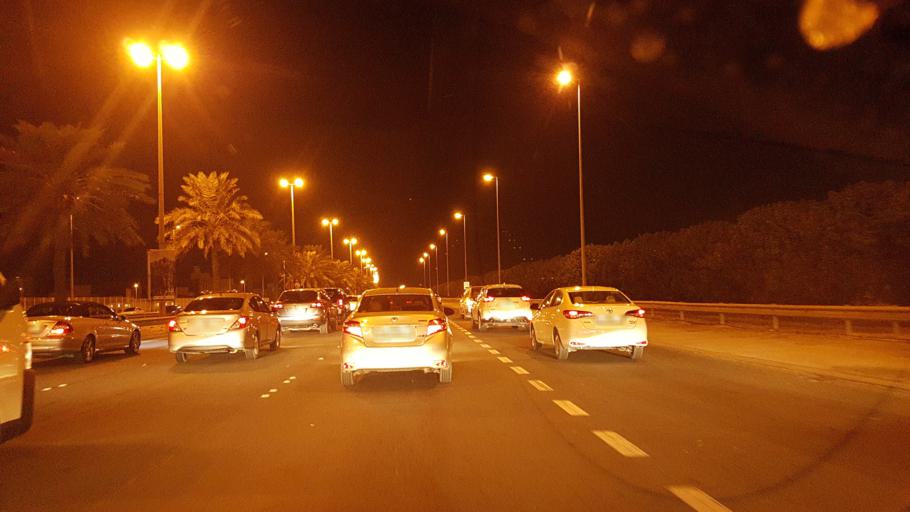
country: BH
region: Central Governorate
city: Madinat Hamad
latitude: 26.1475
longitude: 50.5095
